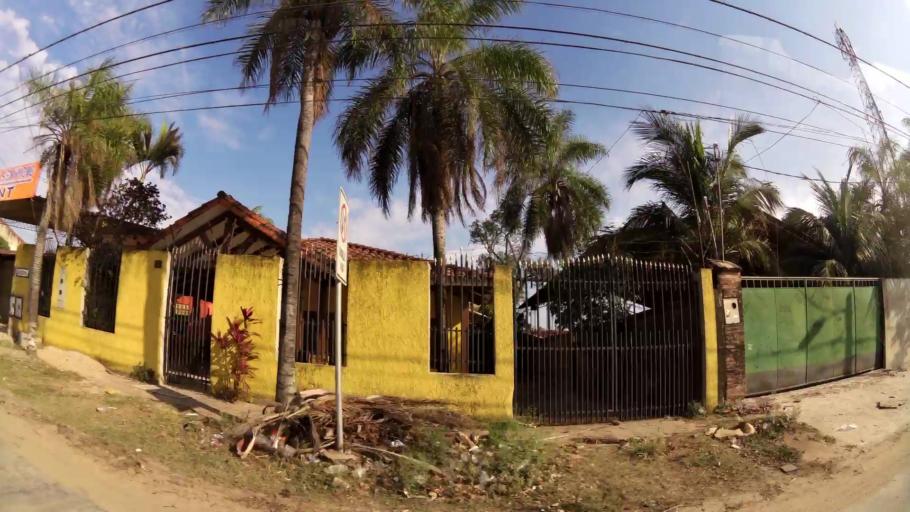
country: BO
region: Santa Cruz
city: Santa Cruz de la Sierra
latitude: -17.7394
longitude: -63.1446
